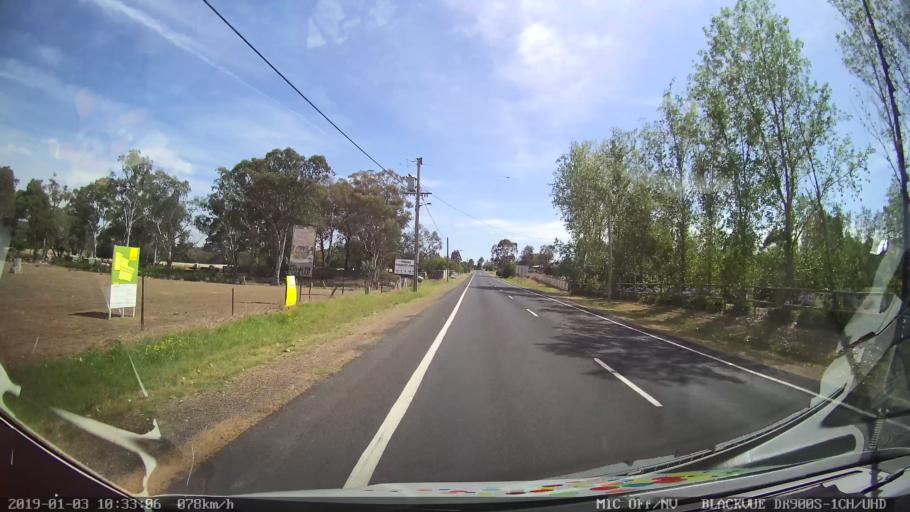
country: AU
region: New South Wales
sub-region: Young
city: Young
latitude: -34.3317
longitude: 148.2856
